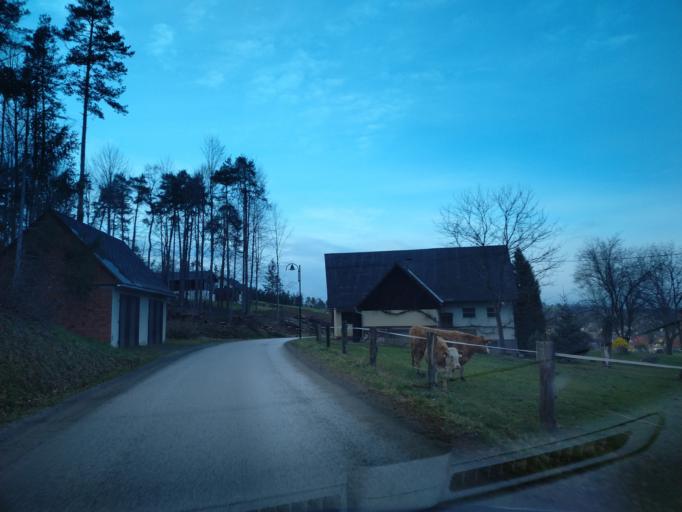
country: AT
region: Styria
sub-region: Politischer Bezirk Deutschlandsberg
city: Pitschgau
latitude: 46.6835
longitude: 15.2647
